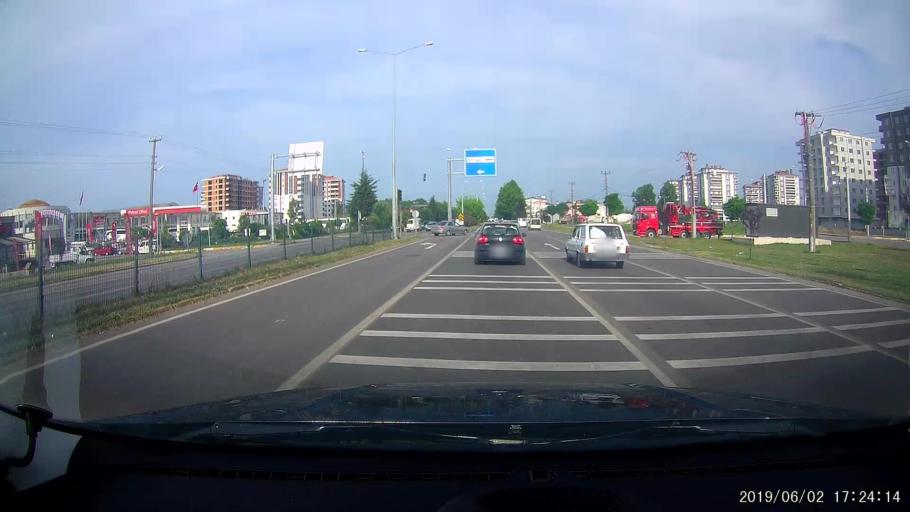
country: TR
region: Samsun
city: Carsamba
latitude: 41.2058
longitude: 36.6988
